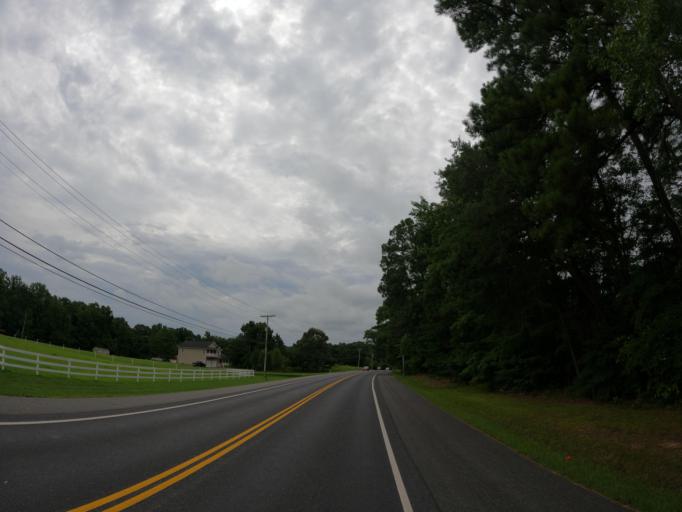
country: US
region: Maryland
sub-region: Saint Mary's County
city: Lexington Park
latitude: 38.2023
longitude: -76.5107
